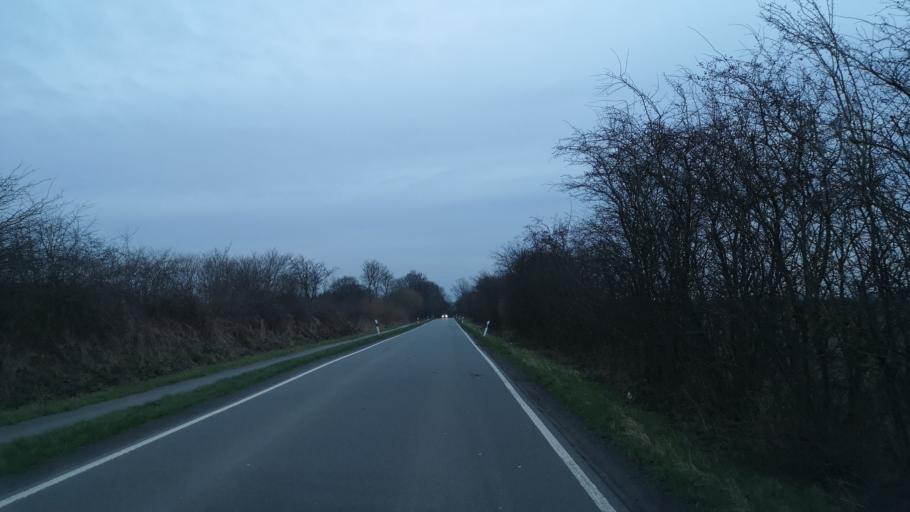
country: DE
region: Schleswig-Holstein
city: Satrup
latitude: 54.6990
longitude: 9.6248
